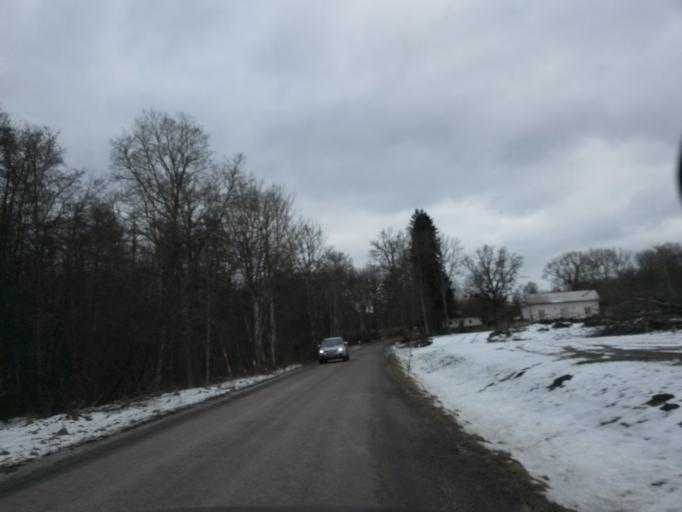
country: SE
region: Vaestra Goetaland
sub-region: Vargarda Kommun
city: Vargarda
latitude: 58.0308
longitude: 12.8601
